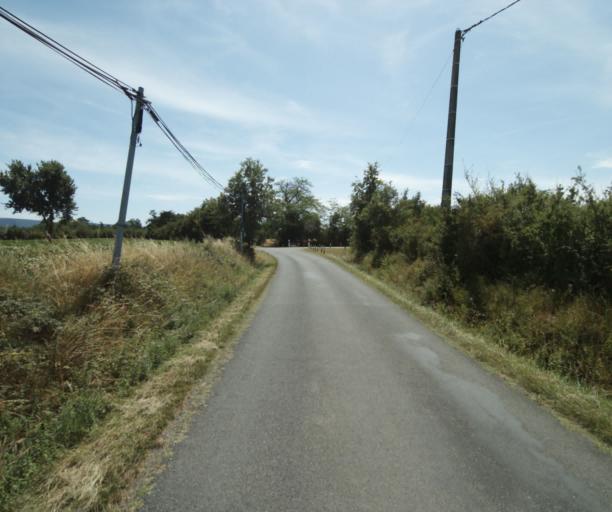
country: FR
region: Midi-Pyrenees
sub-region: Departement de la Haute-Garonne
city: Revel
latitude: 43.4996
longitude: 2.0031
